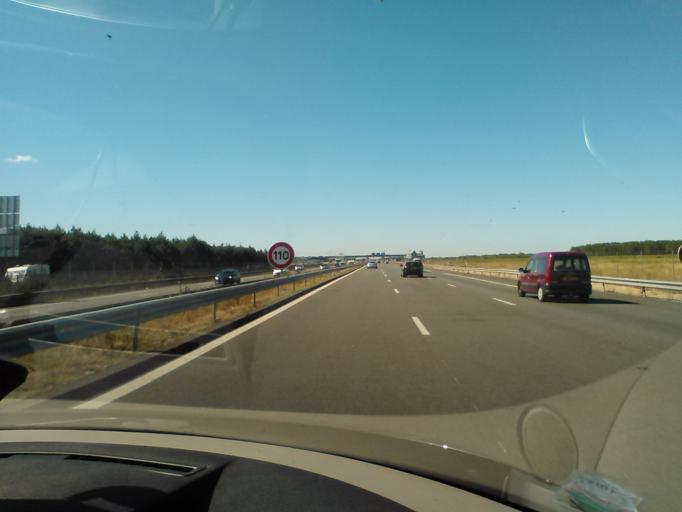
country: FR
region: Aquitaine
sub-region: Departement des Landes
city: Pissos
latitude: 44.3536
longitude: -0.8561
